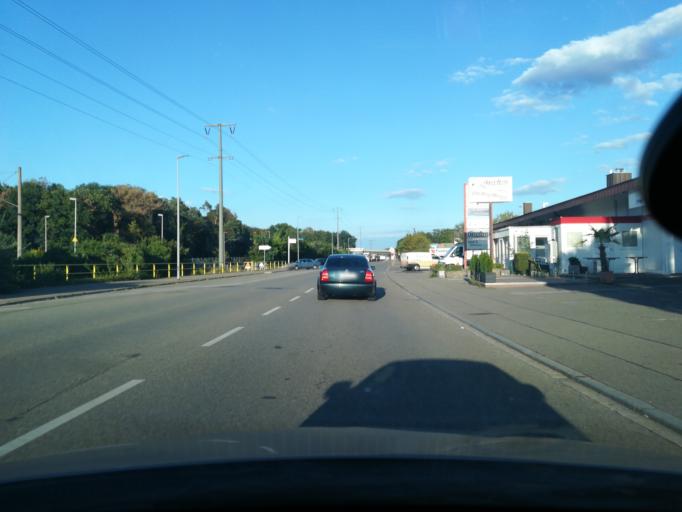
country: DE
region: Baden-Wuerttemberg
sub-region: Freiburg Region
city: Singen
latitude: 47.7591
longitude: 8.8723
